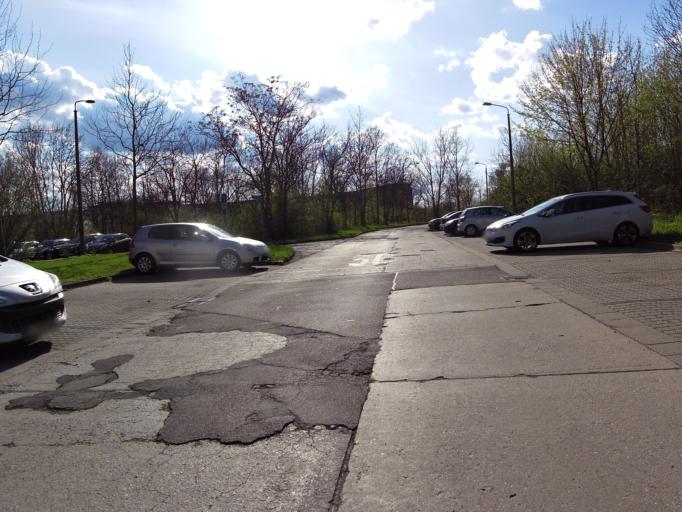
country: DE
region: Saxony
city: Markranstadt
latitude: 51.3288
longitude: 12.2861
